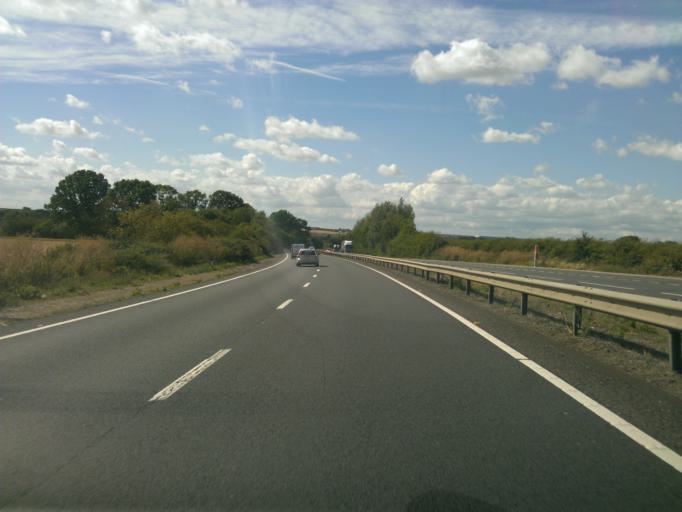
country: GB
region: England
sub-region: Northamptonshire
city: Thrapston
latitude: 52.3838
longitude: -0.4893
